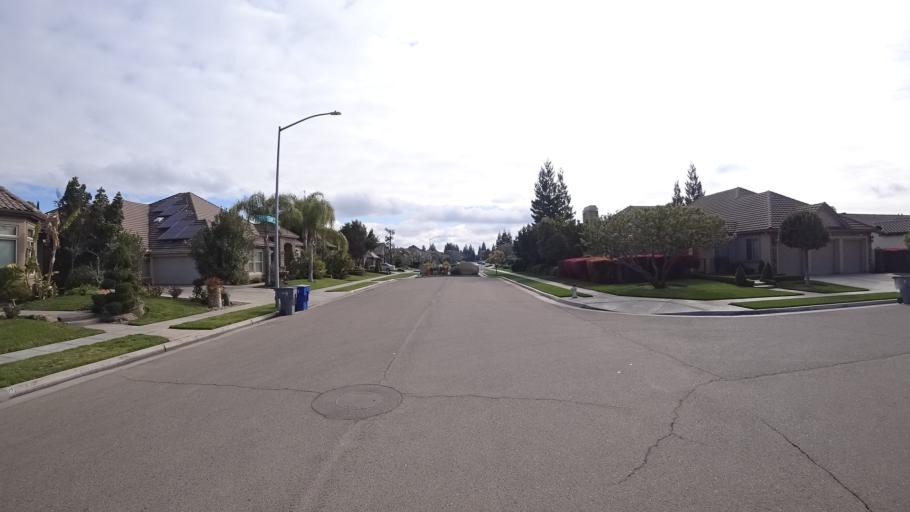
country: US
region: California
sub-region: Fresno County
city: West Park
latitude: 36.8284
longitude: -119.8666
